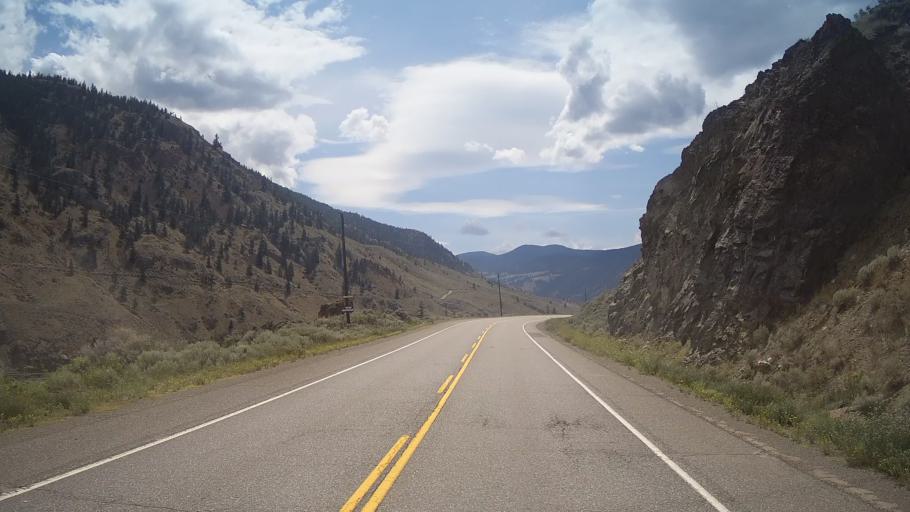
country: CA
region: British Columbia
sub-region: Thompson-Nicola Regional District
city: Ashcroft
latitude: 50.4622
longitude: -121.3012
